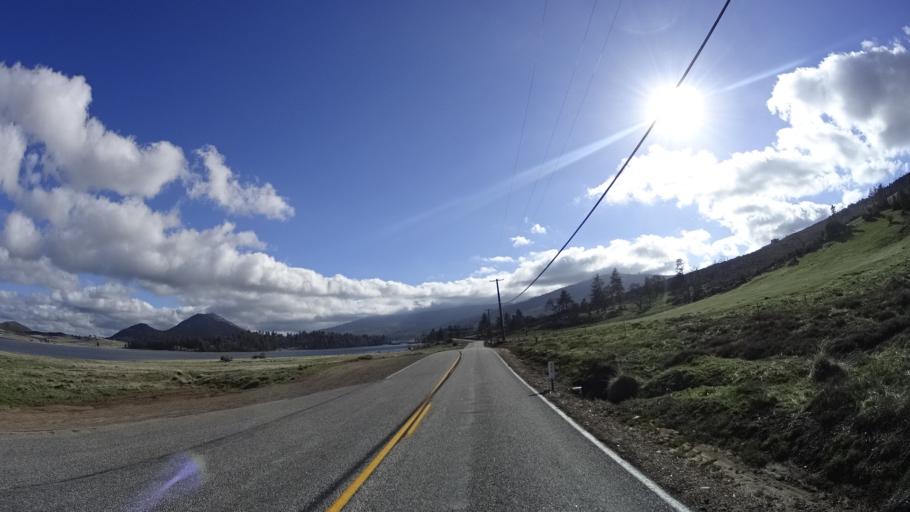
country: US
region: California
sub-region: San Diego County
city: Julian
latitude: 32.9964
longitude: -116.5693
